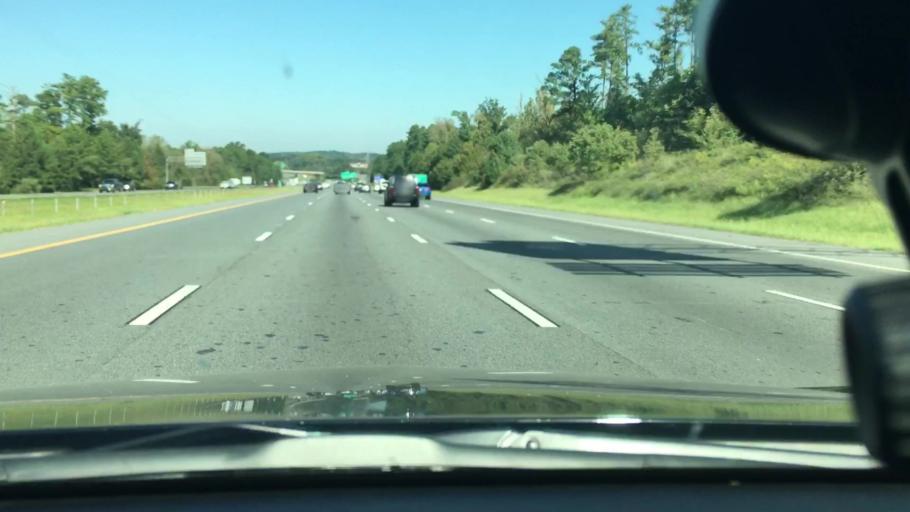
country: US
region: North Carolina
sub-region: Cabarrus County
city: Harrisburg
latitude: 35.3227
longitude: -80.7141
